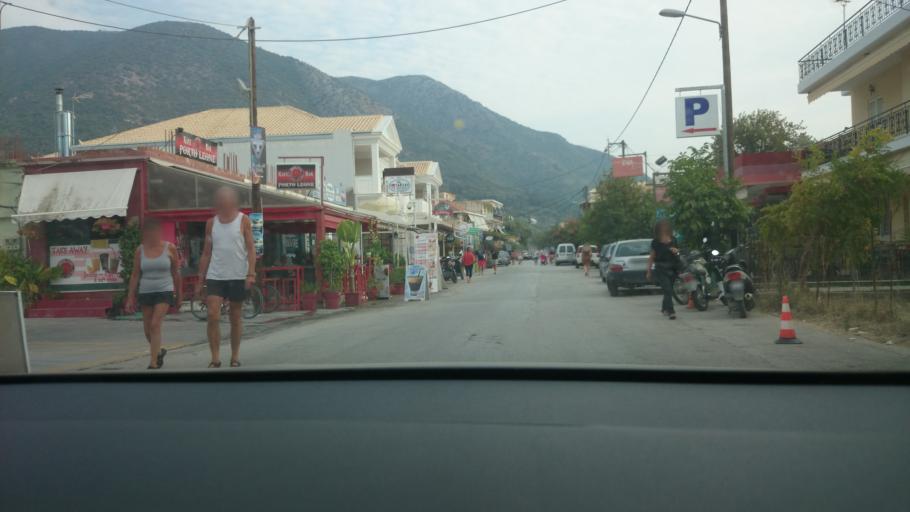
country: GR
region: Ionian Islands
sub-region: Lefkada
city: Nidri
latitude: 38.7107
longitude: 20.7137
